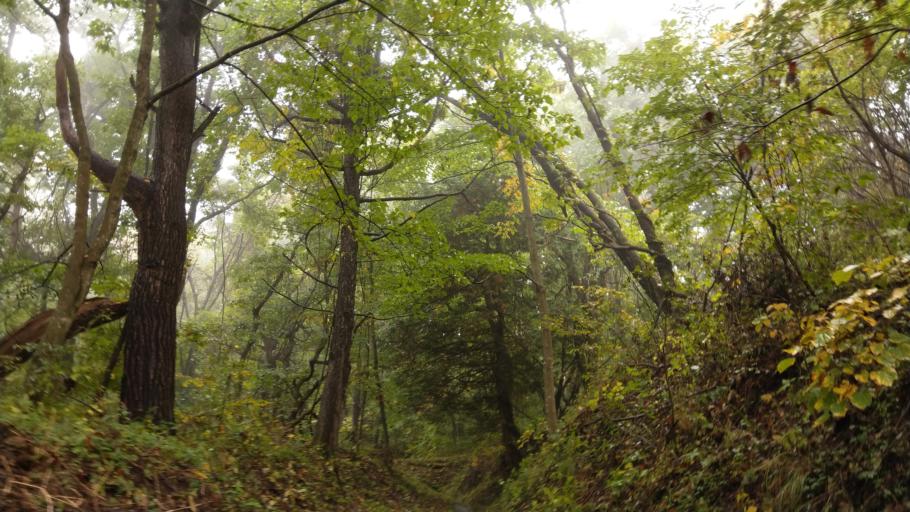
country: JP
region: Nagano
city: Komoro
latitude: 36.3641
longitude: 138.4438
